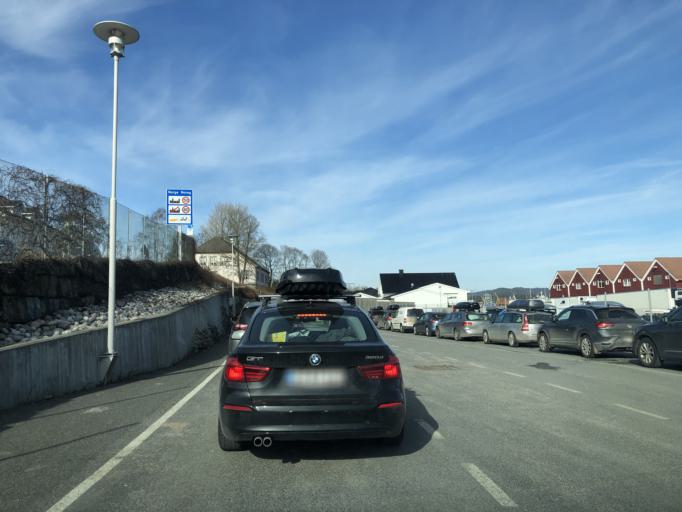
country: NO
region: Telemark
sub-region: Bamble
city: Langesund
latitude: 59.0068
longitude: 9.7464
